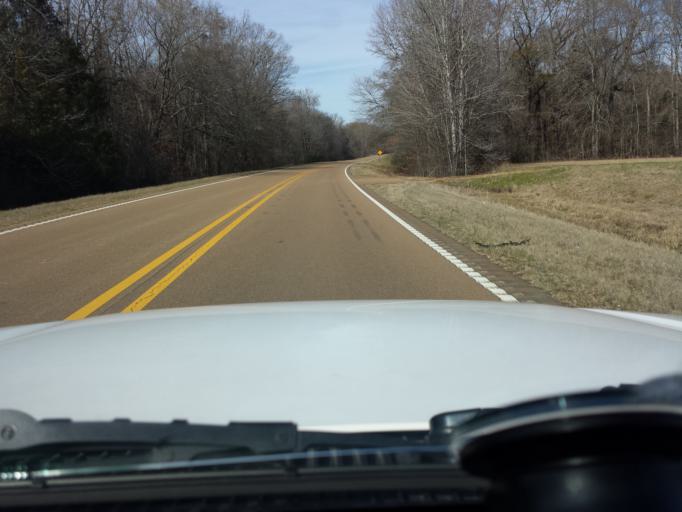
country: US
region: Mississippi
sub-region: Madison County
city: Canton
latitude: 32.7045
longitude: -90.0915
